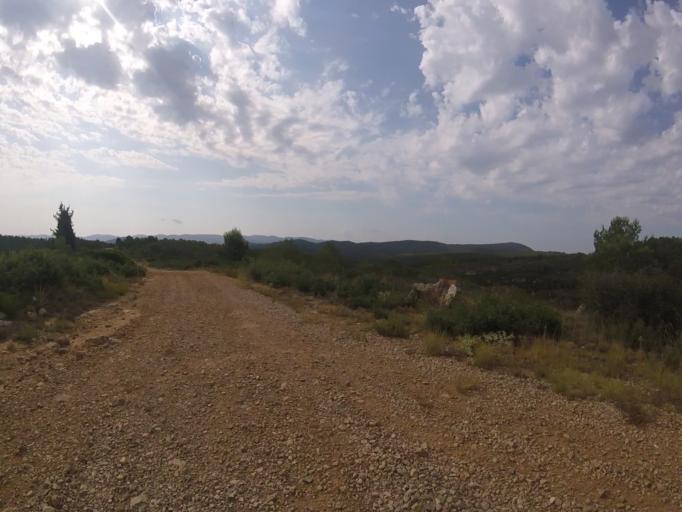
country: ES
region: Valencia
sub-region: Provincia de Castello
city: Alcala de Xivert
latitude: 40.3792
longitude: 0.2070
